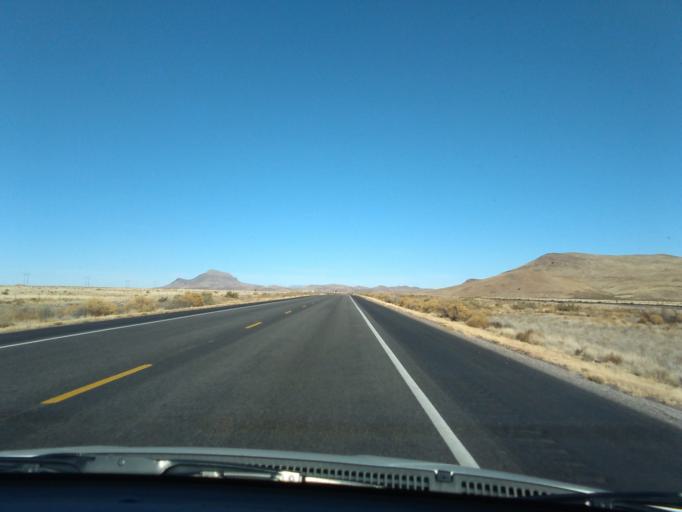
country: US
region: New Mexico
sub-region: Dona Ana County
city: Hatch
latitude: 32.5271
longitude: -107.4922
